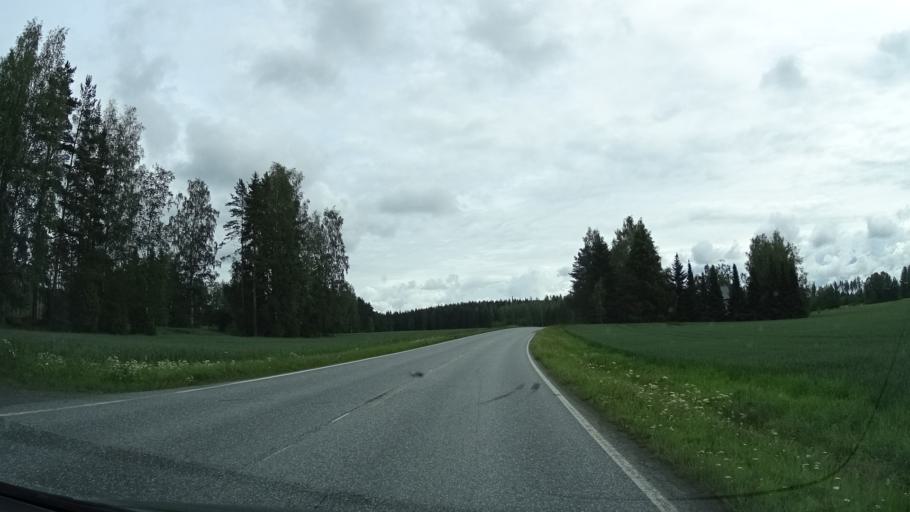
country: FI
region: Pirkanmaa
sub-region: Etelae-Pirkanmaa
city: Urjala
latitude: 61.0907
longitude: 23.5095
